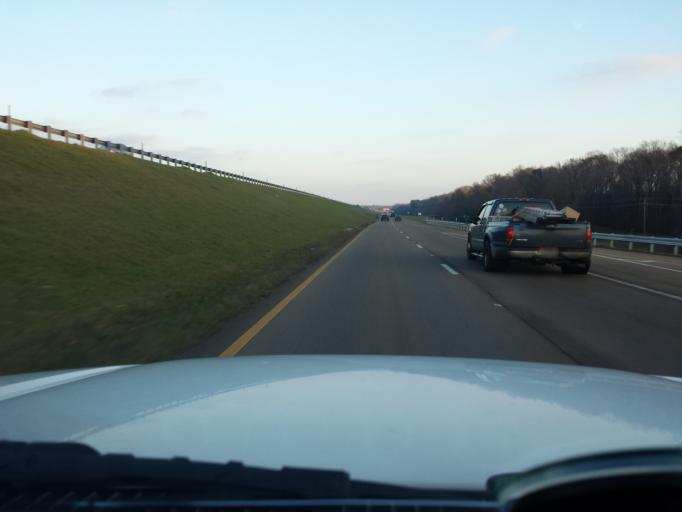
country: US
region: Mississippi
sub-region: Madison County
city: Ridgeland
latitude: 32.3951
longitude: -90.0613
